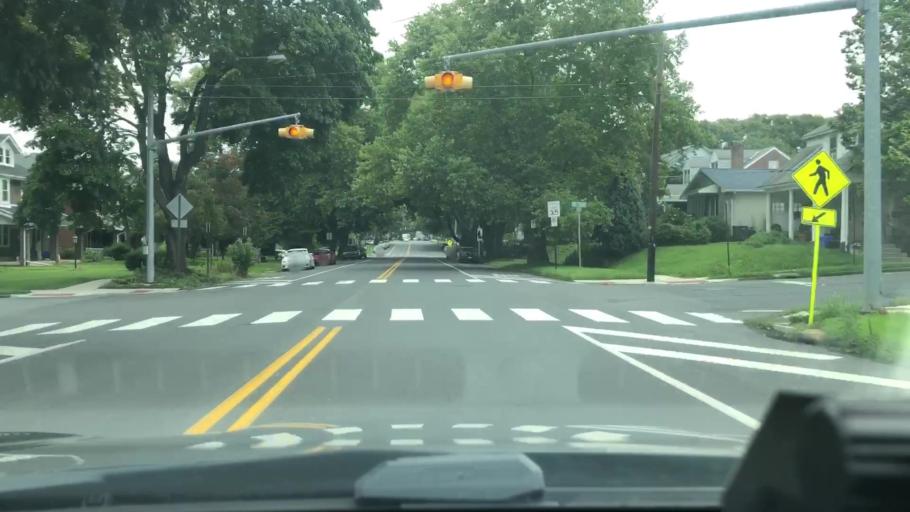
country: US
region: Pennsylvania
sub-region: Lehigh County
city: Fountain Hill
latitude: 40.6254
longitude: -75.3994
